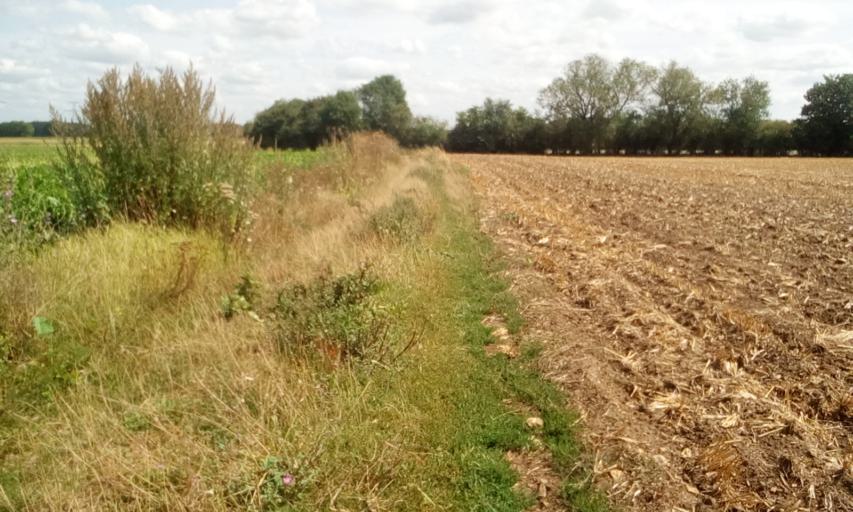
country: FR
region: Lower Normandy
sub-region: Departement du Calvados
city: Bellengreville
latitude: 49.1314
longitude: -0.2068
